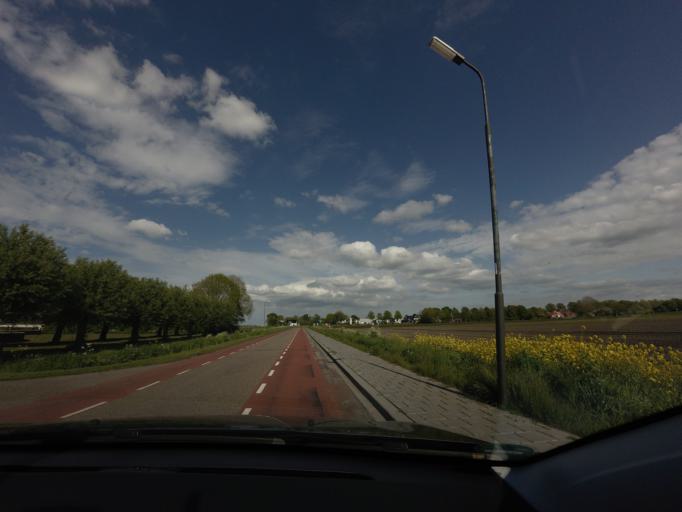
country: NL
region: North Holland
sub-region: Gemeente Heerhugowaard
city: Heerhugowaard
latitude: 52.6344
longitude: 4.8878
